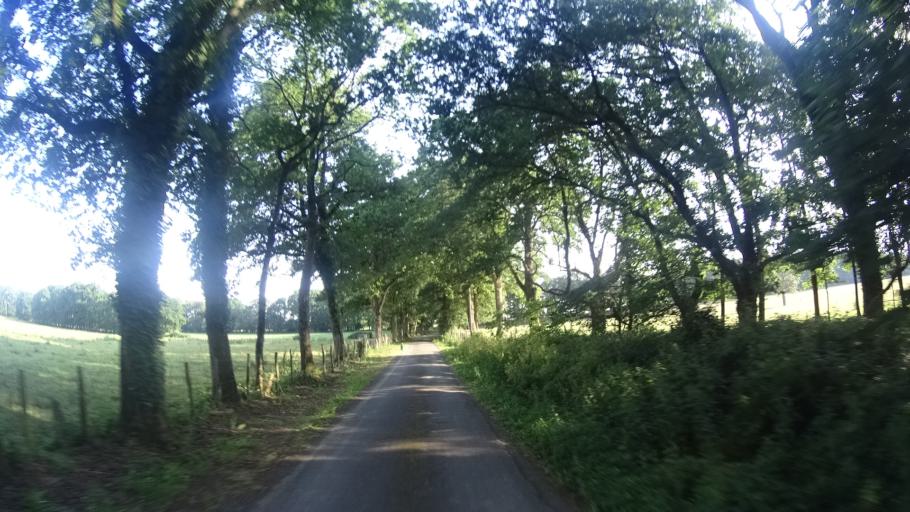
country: FR
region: Brittany
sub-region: Departement d'Ille-et-Vilaine
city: Bains-sur-Oust
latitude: 47.6778
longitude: -2.0699
